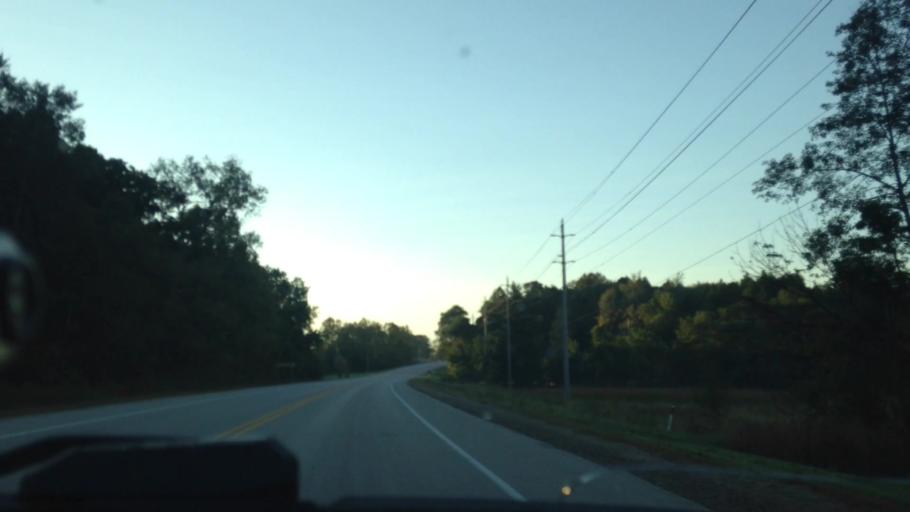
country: US
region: Wisconsin
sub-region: Washington County
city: Newburg
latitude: 43.4237
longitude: -88.0310
